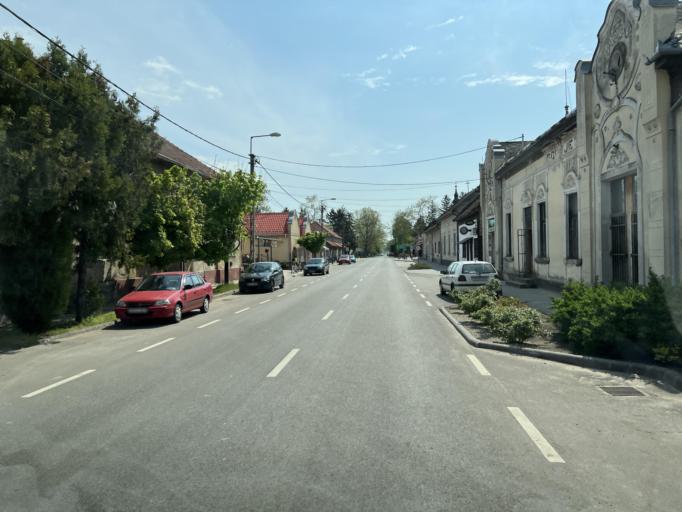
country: HU
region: Pest
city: Kocser
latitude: 47.0024
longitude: 19.9210
